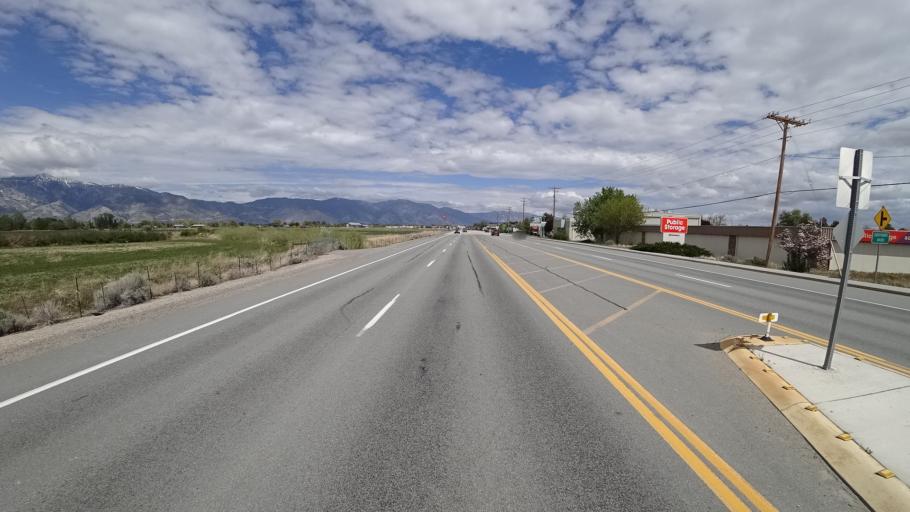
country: US
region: Nevada
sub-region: Douglas County
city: Gardnerville
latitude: 38.9250
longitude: -119.7275
